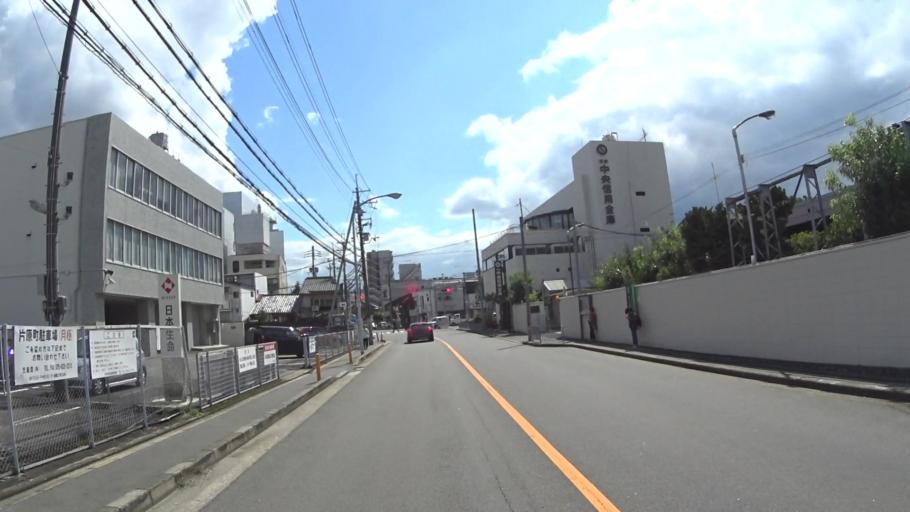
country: JP
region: Kyoto
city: Uji
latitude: 34.9337
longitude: 135.7583
